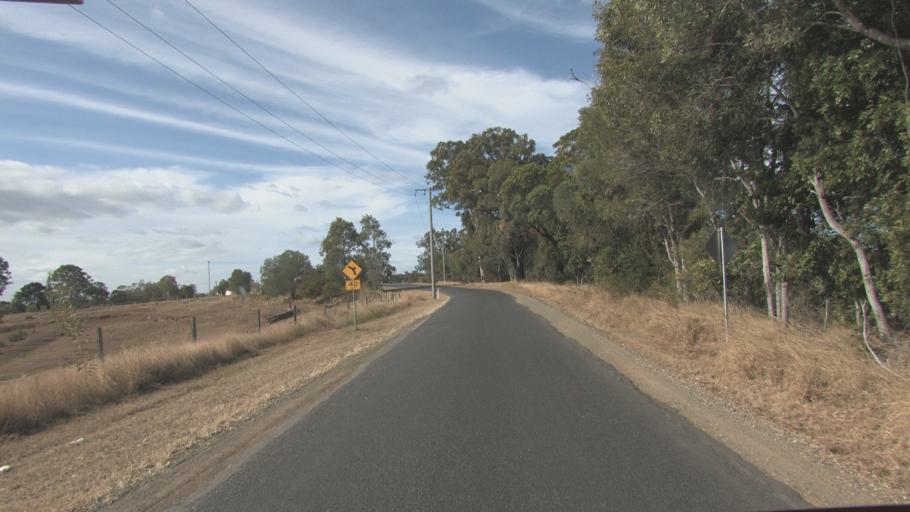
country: AU
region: Queensland
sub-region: Logan
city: Cedar Vale
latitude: -27.9006
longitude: 153.0161
